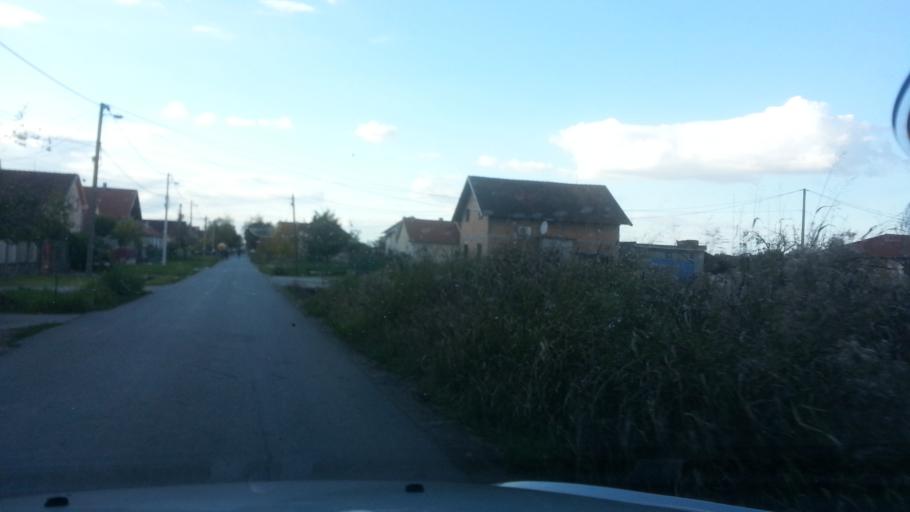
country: RS
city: Novi Banovci
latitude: 44.9063
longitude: 20.2686
